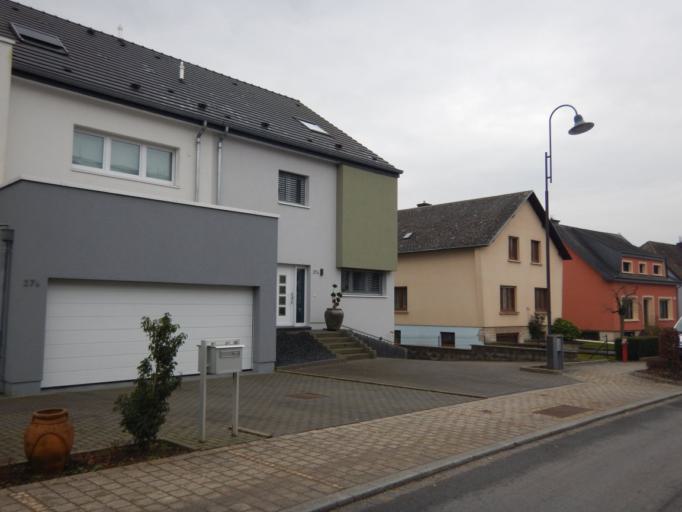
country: LU
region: Luxembourg
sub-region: Canton de Capellen
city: Koerich
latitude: 49.6699
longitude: 5.9445
